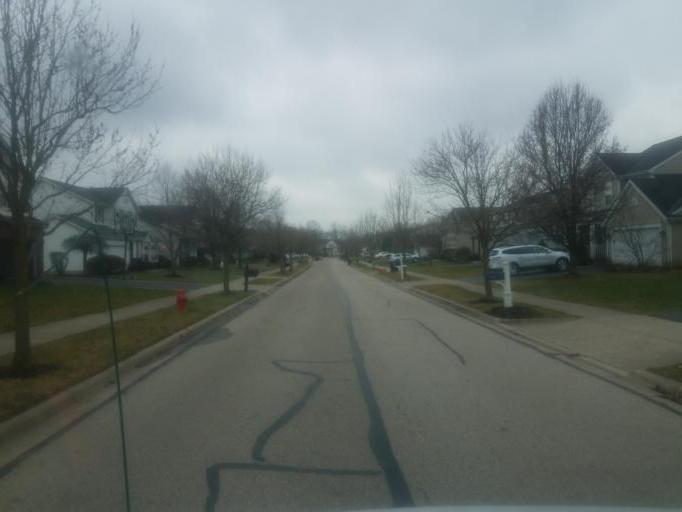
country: US
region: Ohio
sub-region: Franklin County
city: Westerville
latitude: 40.1370
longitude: -82.9596
